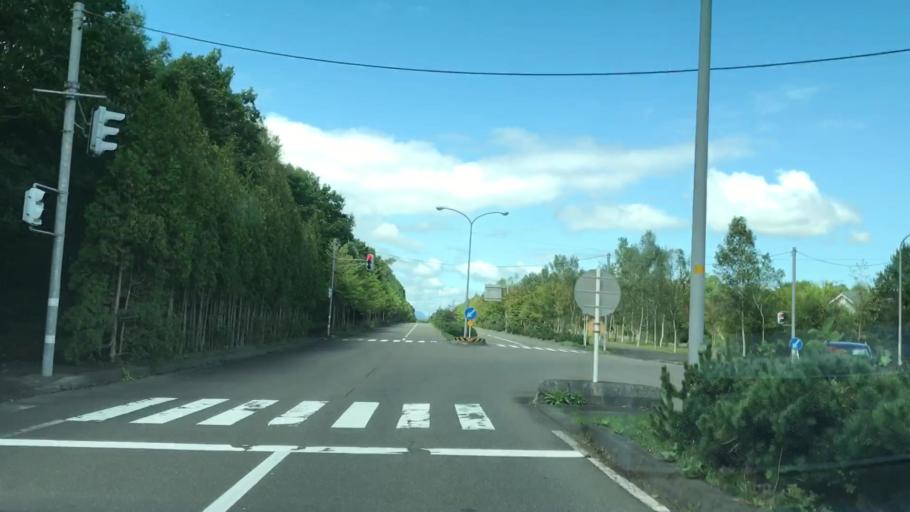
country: JP
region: Hokkaido
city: Chitose
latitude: 42.7748
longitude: 141.5998
